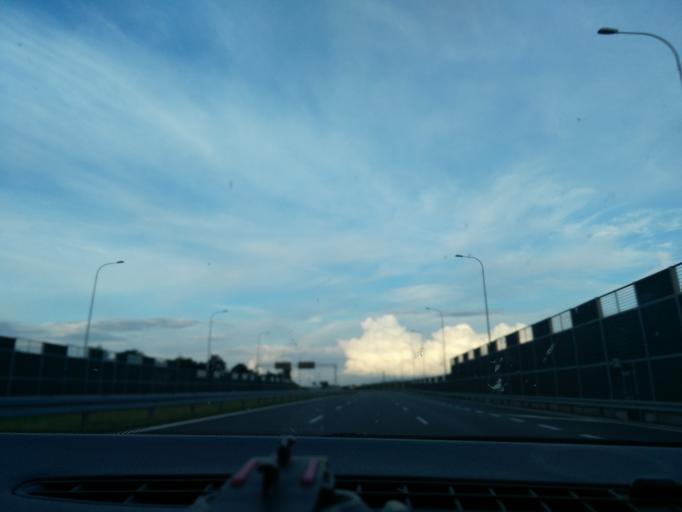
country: PL
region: Lublin Voivodeship
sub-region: Powiat lubelski
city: Lublin
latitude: 51.2992
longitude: 22.5200
